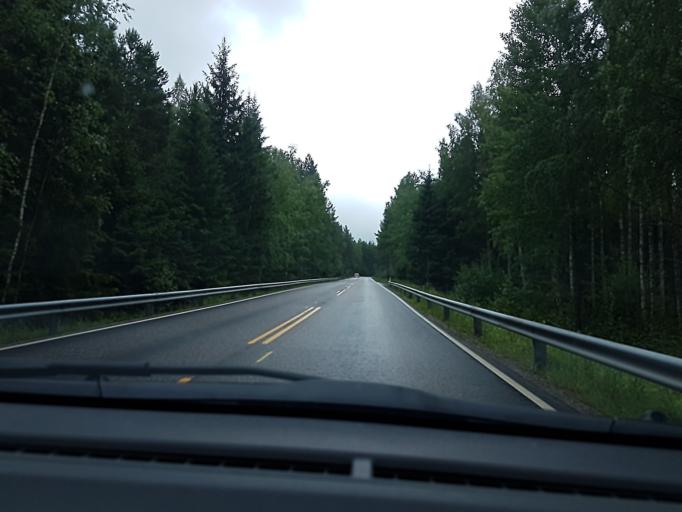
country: FI
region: Uusimaa
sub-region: Helsinki
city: Pornainen
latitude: 60.4621
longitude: 25.3895
